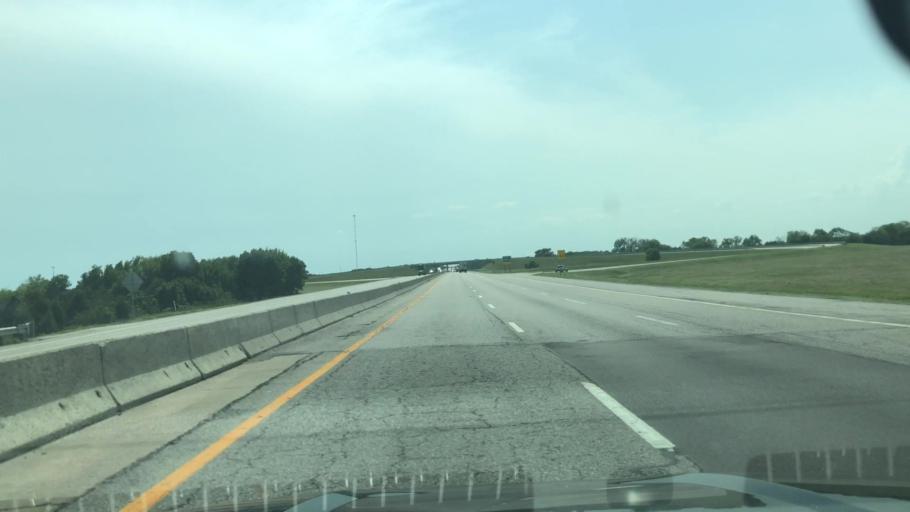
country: US
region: Oklahoma
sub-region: Ottawa County
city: Afton
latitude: 36.7244
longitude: -94.9298
